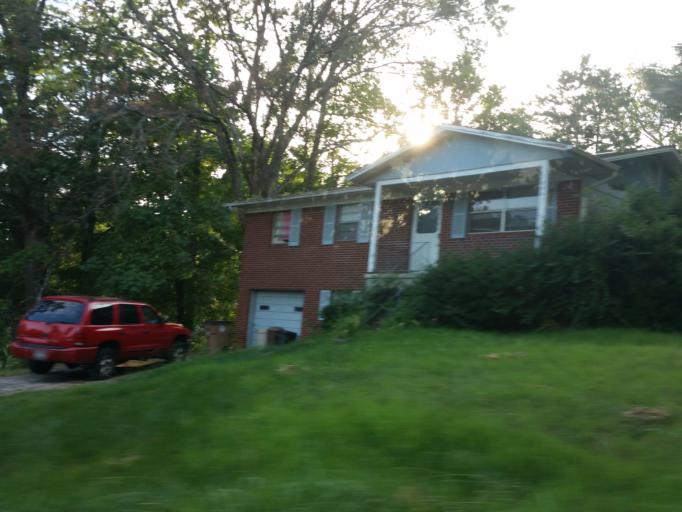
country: US
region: Tennessee
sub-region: Knox County
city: Knoxville
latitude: 36.0424
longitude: -83.9383
